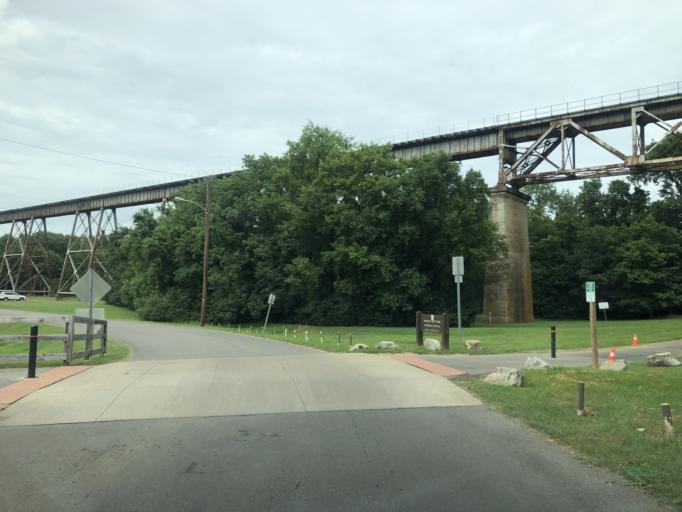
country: US
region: Tennessee
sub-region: Davidson County
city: Nashville
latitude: 36.1656
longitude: -86.7266
